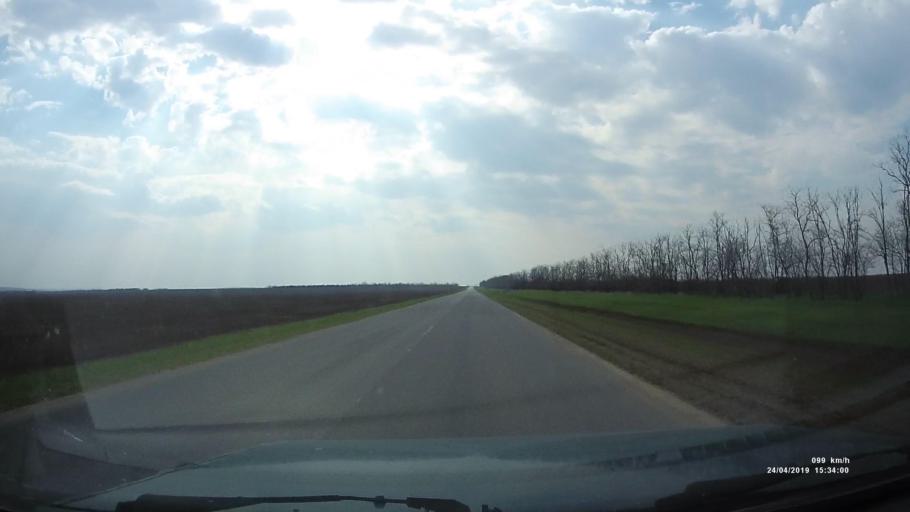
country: RU
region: Kalmykiya
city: Yashalta
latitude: 46.5995
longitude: 42.9260
